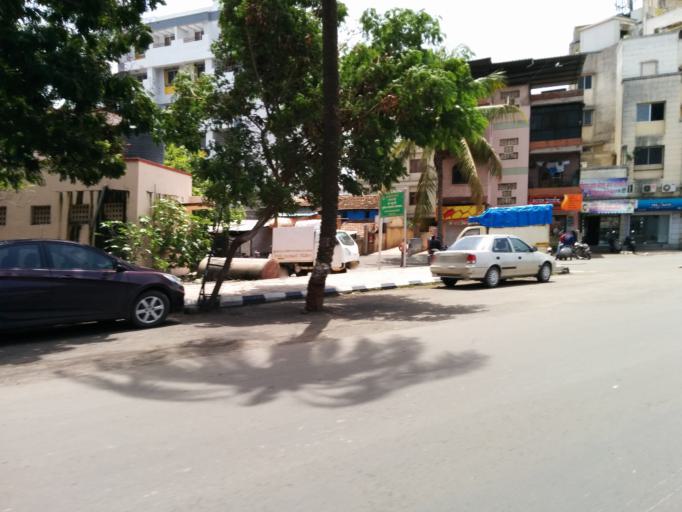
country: IN
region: Maharashtra
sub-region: Pune Division
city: Lohogaon
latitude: 18.5339
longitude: 73.9295
